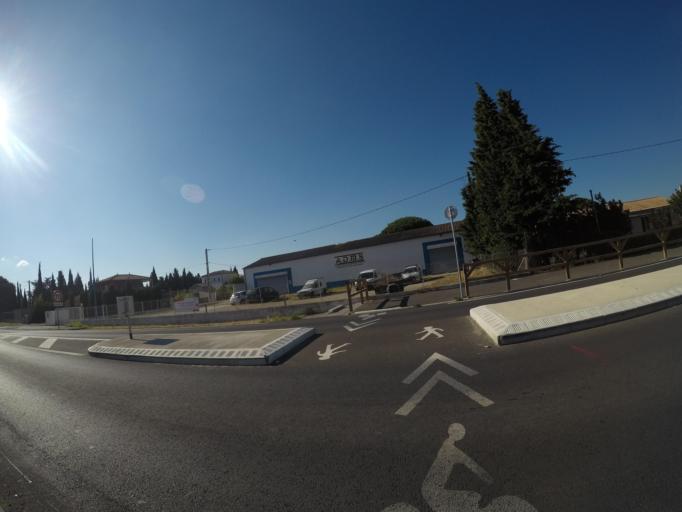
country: FR
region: Languedoc-Roussillon
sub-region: Departement des Pyrenees-Orientales
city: Pezilla-la-Riviere
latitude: 42.6797
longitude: 2.7648
